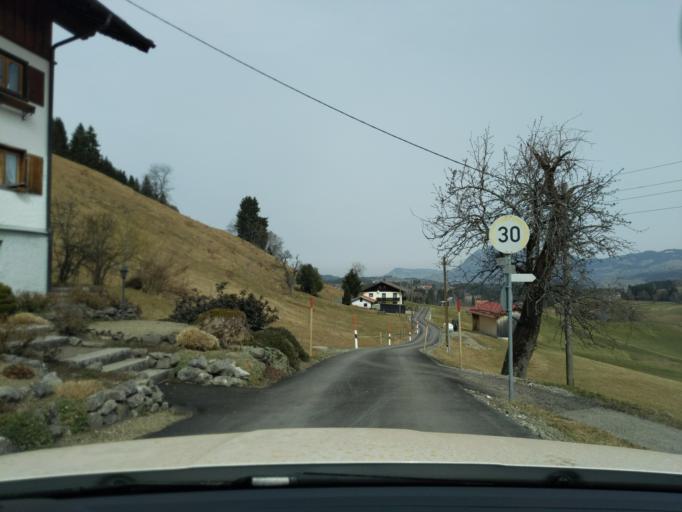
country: DE
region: Bavaria
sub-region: Swabia
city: Obermaiselstein
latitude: 47.4398
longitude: 10.2329
